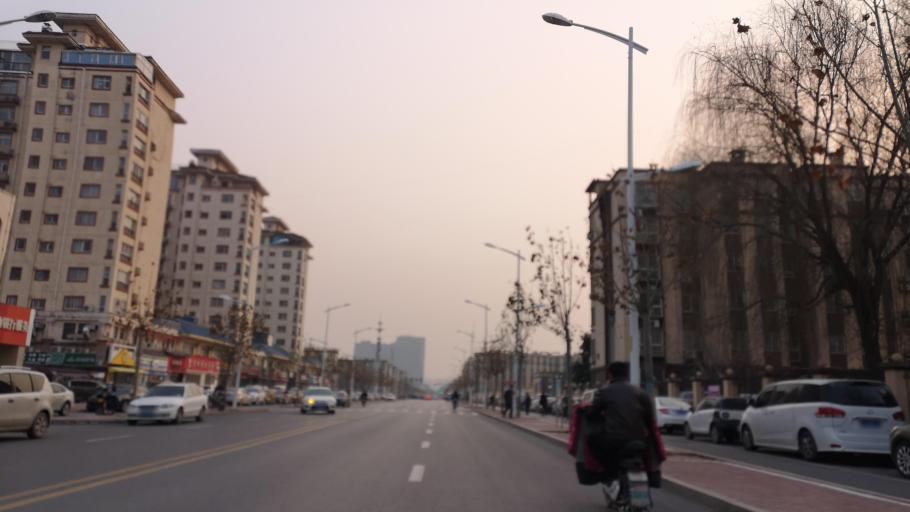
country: CN
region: Henan Sheng
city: Zhongyuanlu
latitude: 35.7858
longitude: 115.0815
